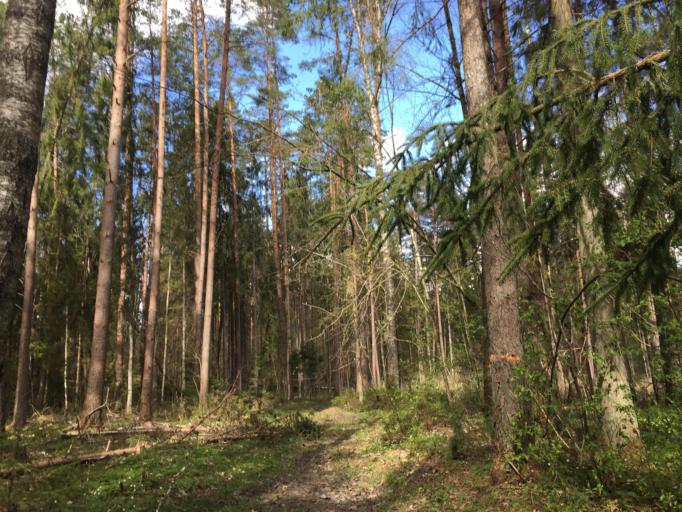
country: LV
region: Baldone
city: Baldone
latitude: 56.7505
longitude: 24.3814
